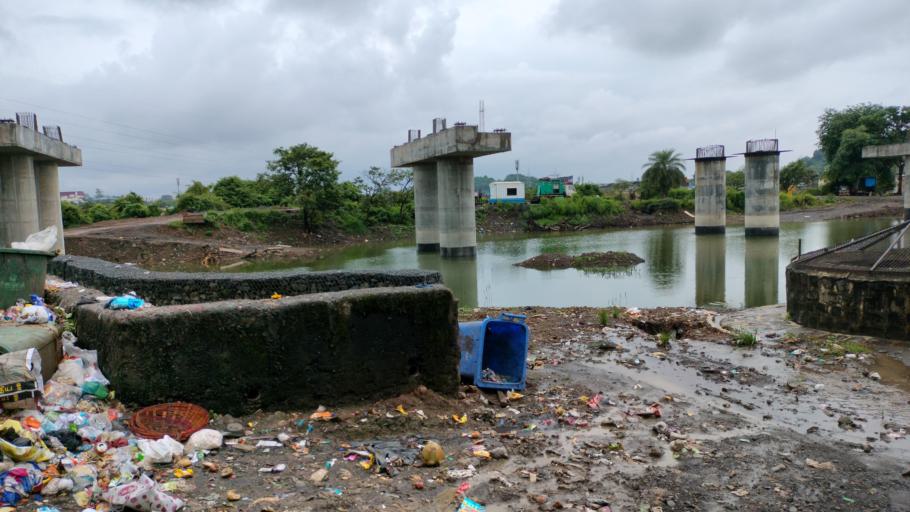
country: IN
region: Maharashtra
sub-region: Thane
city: Virar
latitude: 19.4258
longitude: 72.8480
